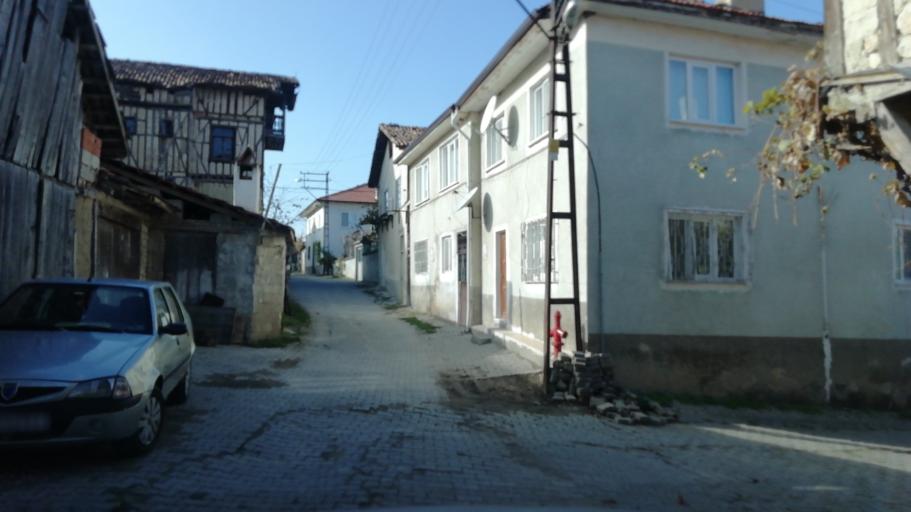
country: TR
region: Karabuk
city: Safranbolu
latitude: 41.2311
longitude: 32.7795
